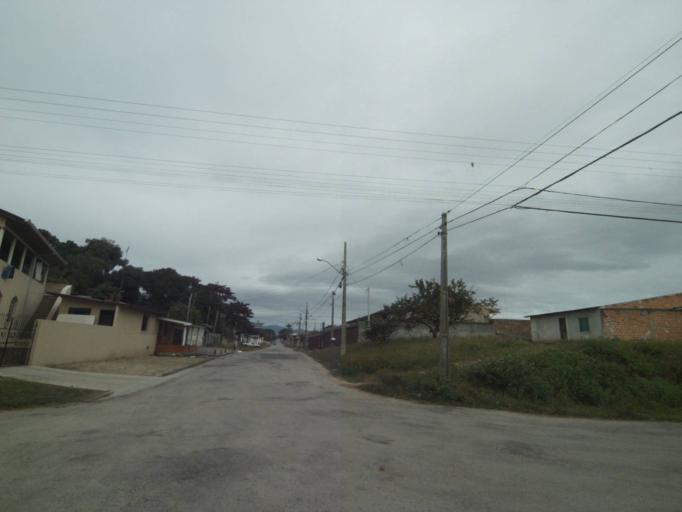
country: BR
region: Parana
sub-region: Paranagua
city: Paranagua
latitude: -25.5185
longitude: -48.5276
